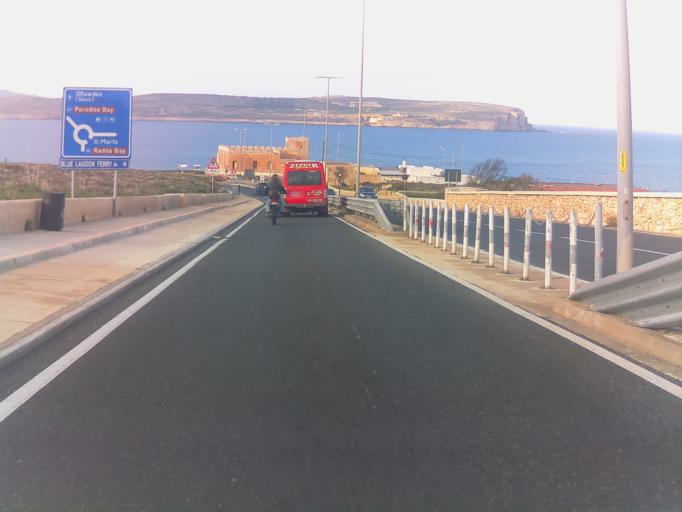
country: MT
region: Il-Mellieha
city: Mellieha
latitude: 35.9842
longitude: 14.3419
